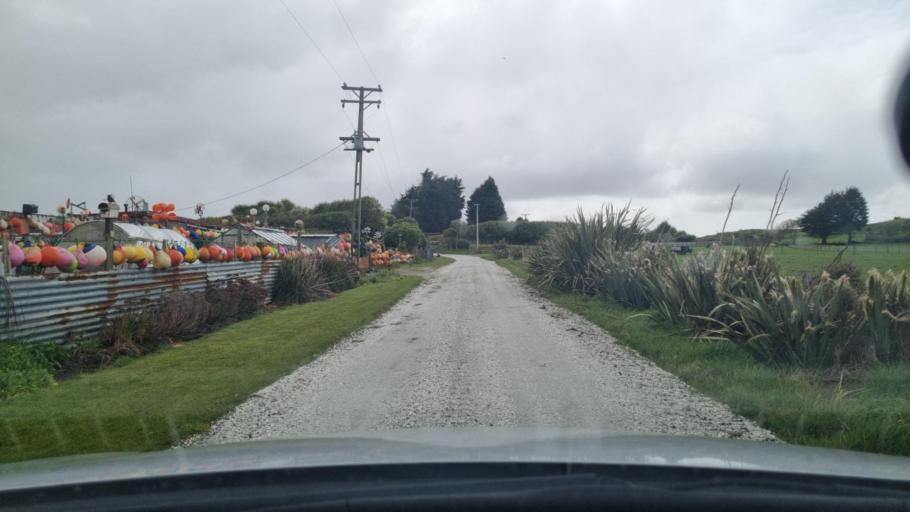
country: NZ
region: Southland
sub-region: Invercargill City
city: Bluff
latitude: -46.5397
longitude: 168.2905
